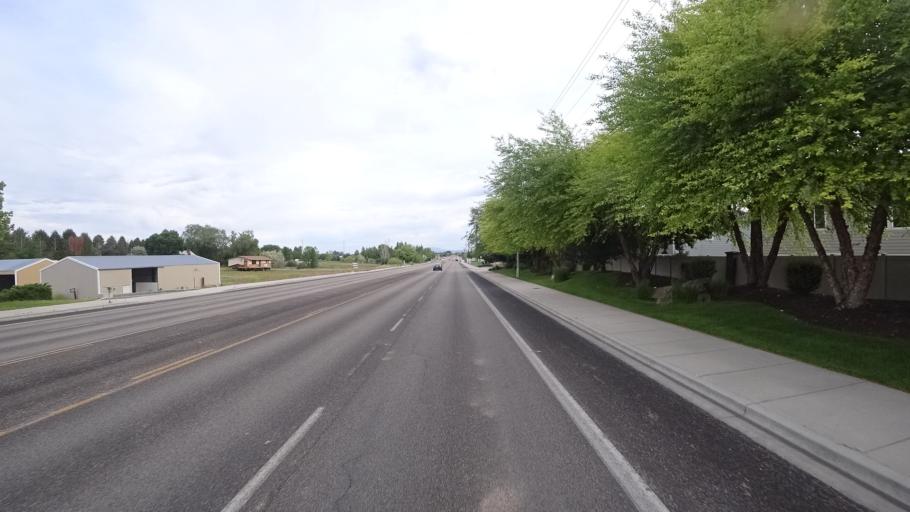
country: US
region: Idaho
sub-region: Ada County
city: Meridian
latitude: 43.6015
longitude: -116.3745
